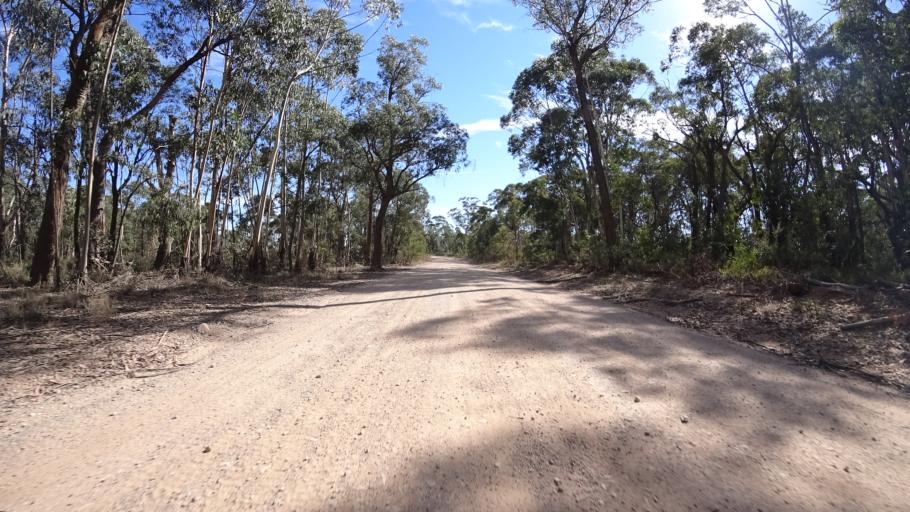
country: AU
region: New South Wales
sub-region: Lithgow
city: Lithgow
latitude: -33.4187
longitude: 150.2041
